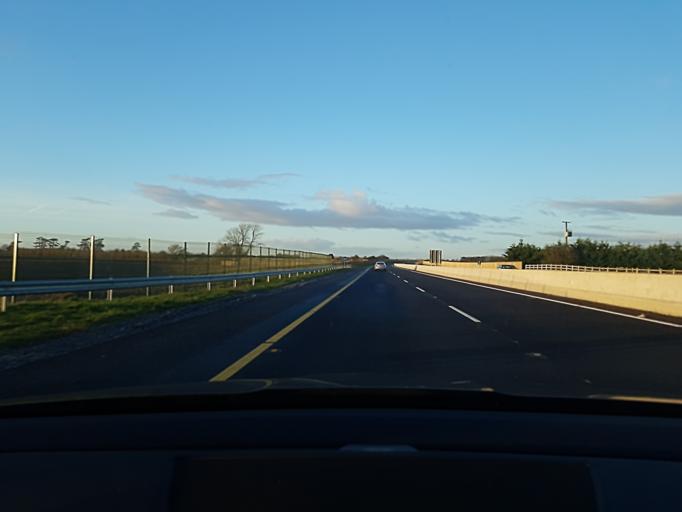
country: IE
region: Connaught
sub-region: County Galway
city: Athenry
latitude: 53.3224
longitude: -8.8027
